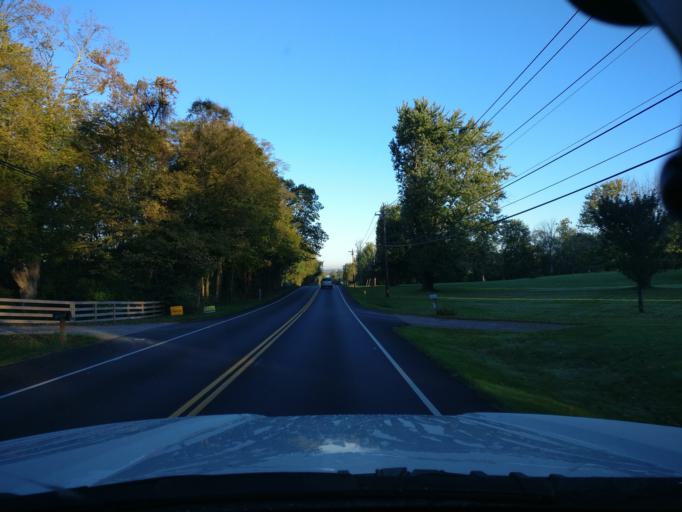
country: US
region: Ohio
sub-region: Warren County
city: Hunter
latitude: 39.5244
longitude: -84.2781
